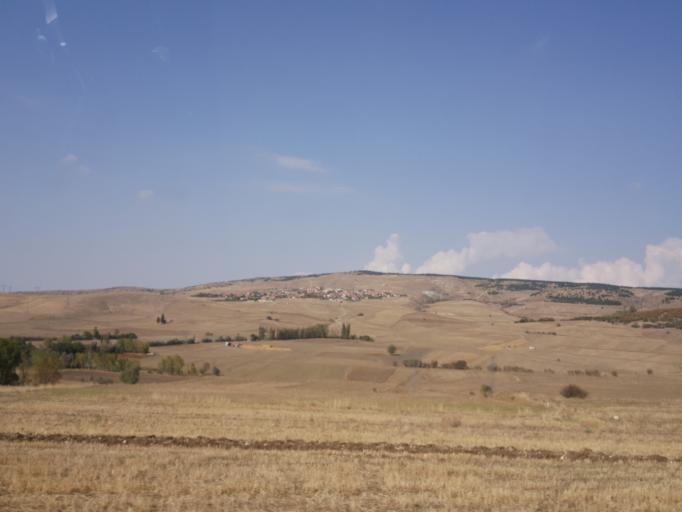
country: TR
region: Corum
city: Bogazkale
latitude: 40.1622
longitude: 34.6585
